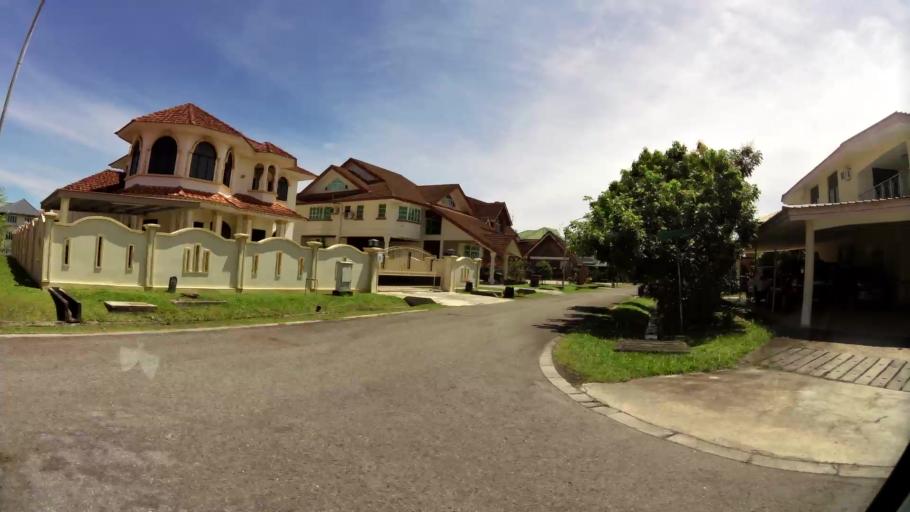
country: BN
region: Belait
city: Kuala Belait
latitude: 4.5854
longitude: 114.2299
